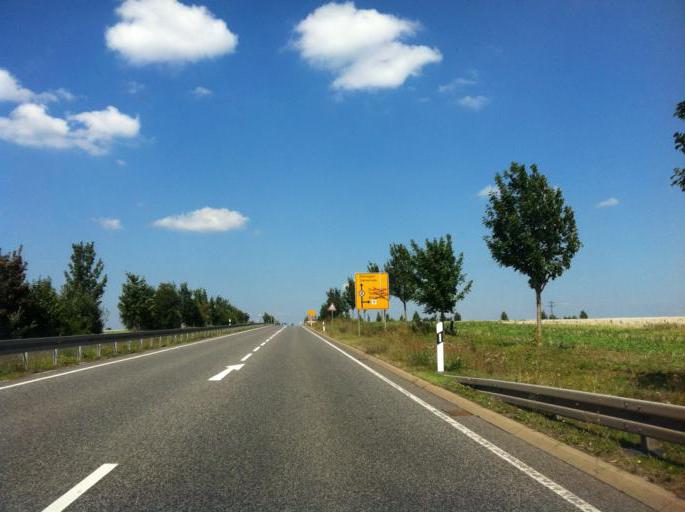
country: DE
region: Thuringia
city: Heilbad Heiligenstadt
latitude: 51.4002
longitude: 10.1287
